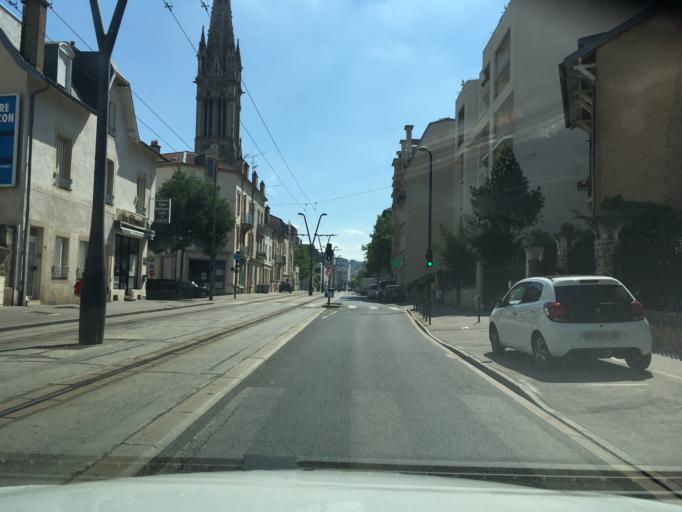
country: FR
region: Lorraine
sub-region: Departement de Meurthe-et-Moselle
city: Nancy
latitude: 48.6748
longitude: 6.1755
